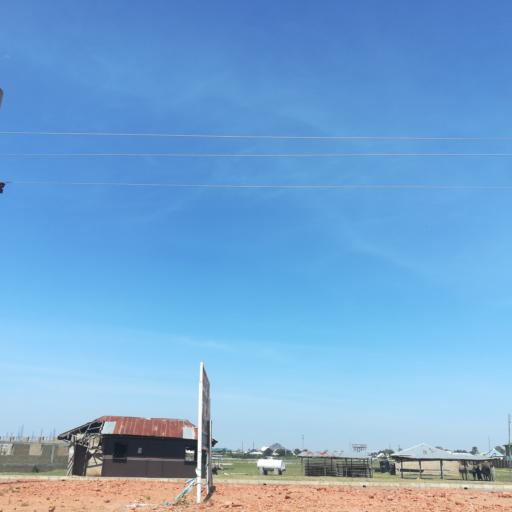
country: NG
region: Plateau
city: Bukuru
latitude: 9.7886
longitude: 8.8735
